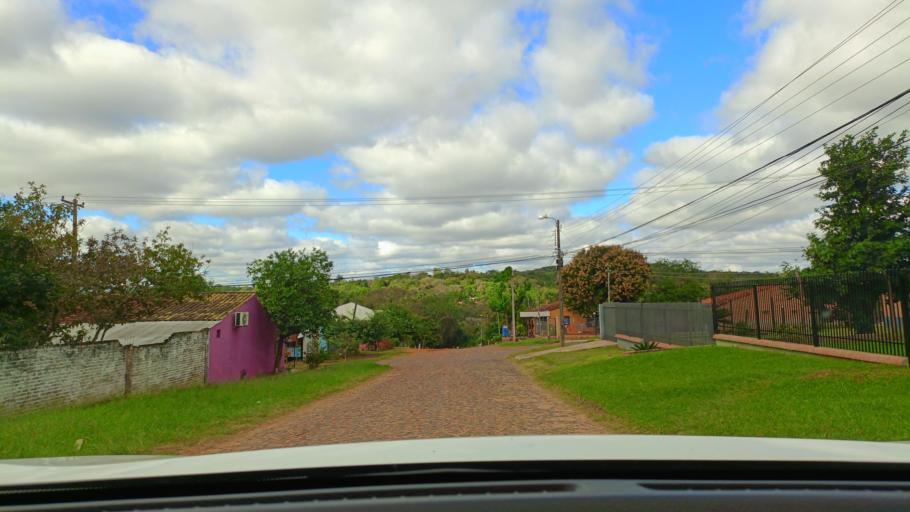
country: PY
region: San Pedro
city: Guayaybi
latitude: -24.6689
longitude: -56.4378
